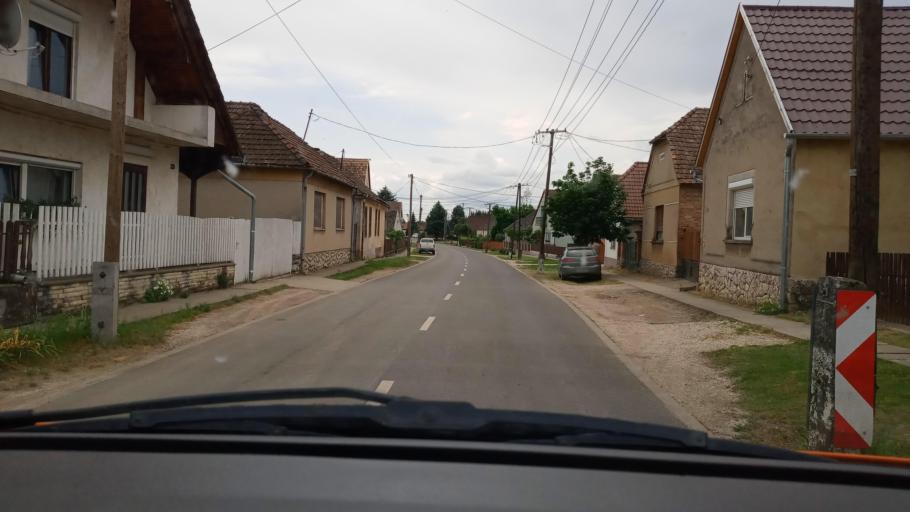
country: HU
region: Baranya
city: Vajszlo
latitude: 45.8572
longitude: 17.9824
